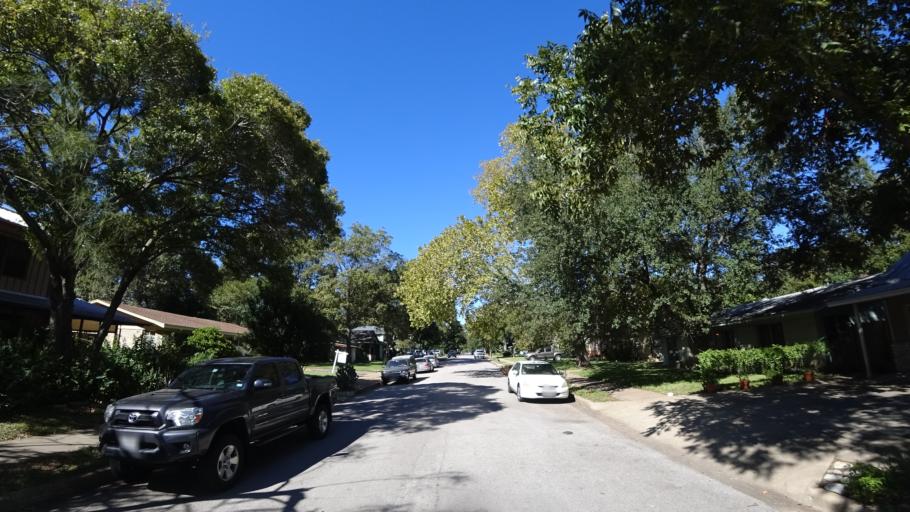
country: US
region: Texas
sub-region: Travis County
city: West Lake Hills
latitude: 30.3257
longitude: -97.7541
